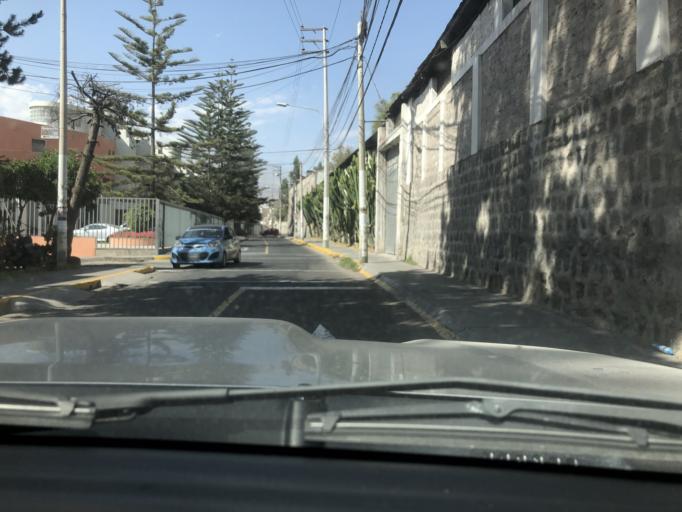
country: PE
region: Arequipa
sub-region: Provincia de Arequipa
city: Arequipa
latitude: -16.3926
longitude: -71.5360
